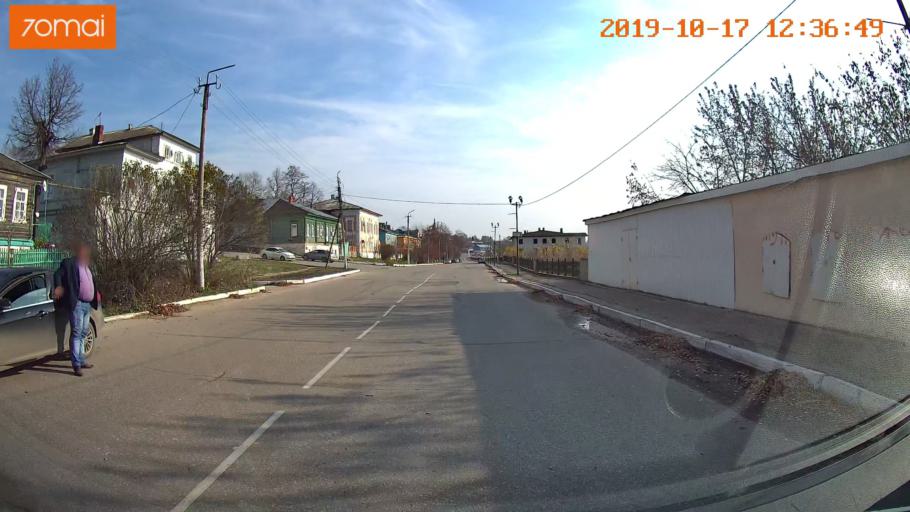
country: RU
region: Rjazan
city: Kasimov
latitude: 54.9387
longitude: 41.3800
